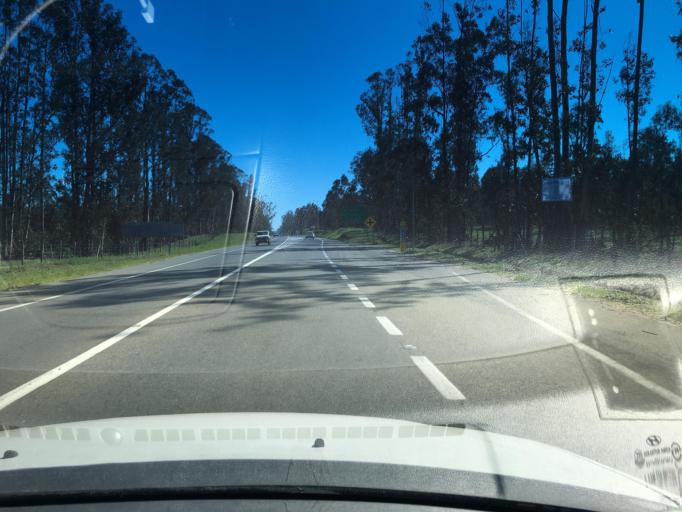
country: CL
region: Valparaiso
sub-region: San Antonio Province
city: El Tabo
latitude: -33.4003
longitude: -71.5858
